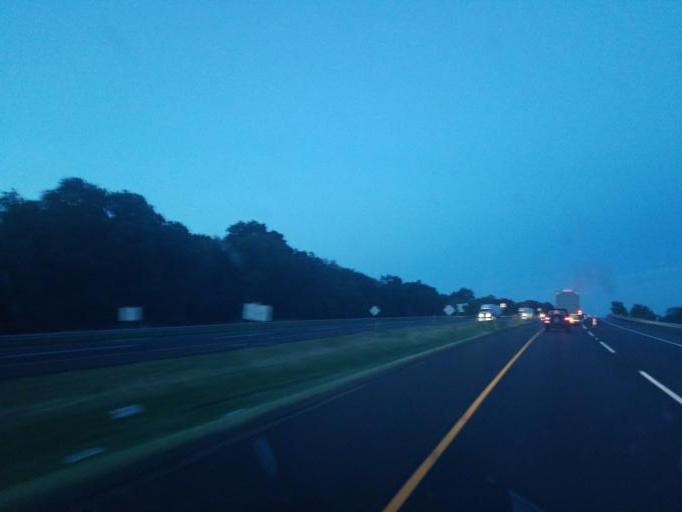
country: US
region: Indiana
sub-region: Saint Joseph County
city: Granger
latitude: 41.7335
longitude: -86.1339
